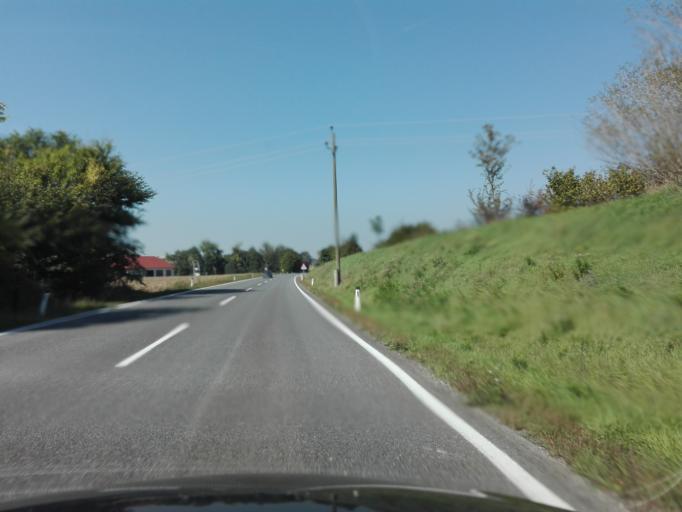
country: AT
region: Upper Austria
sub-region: Politischer Bezirk Linz-Land
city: Horsching
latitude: 48.2225
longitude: 14.1704
